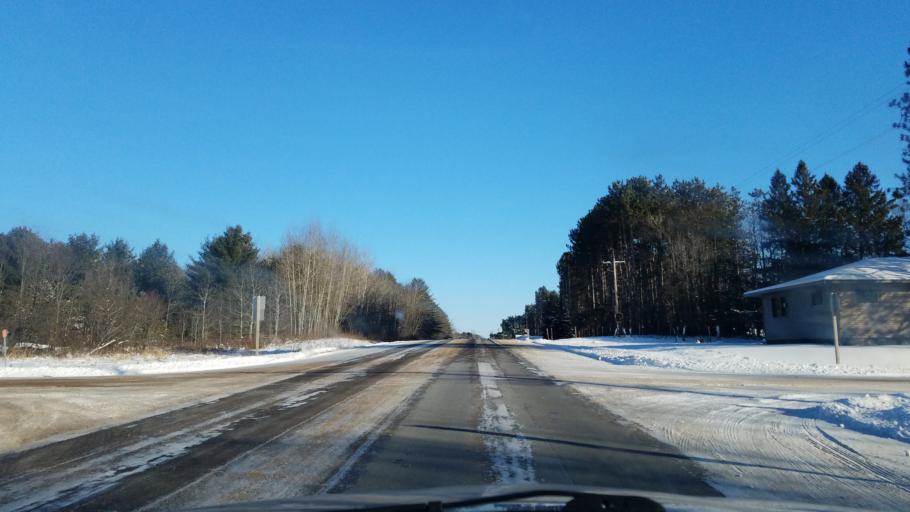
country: US
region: Wisconsin
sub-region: Barron County
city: Rice Lake
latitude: 45.5099
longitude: -91.8277
